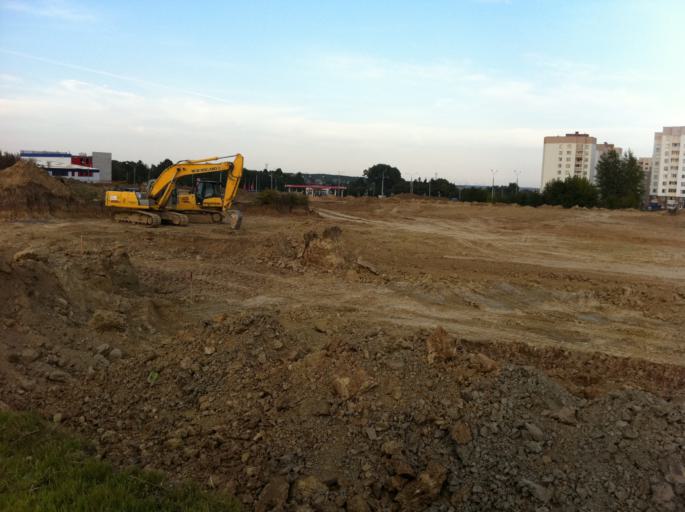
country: BY
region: Grodnenskaya
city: Hrodna
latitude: 53.7150
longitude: 23.8368
